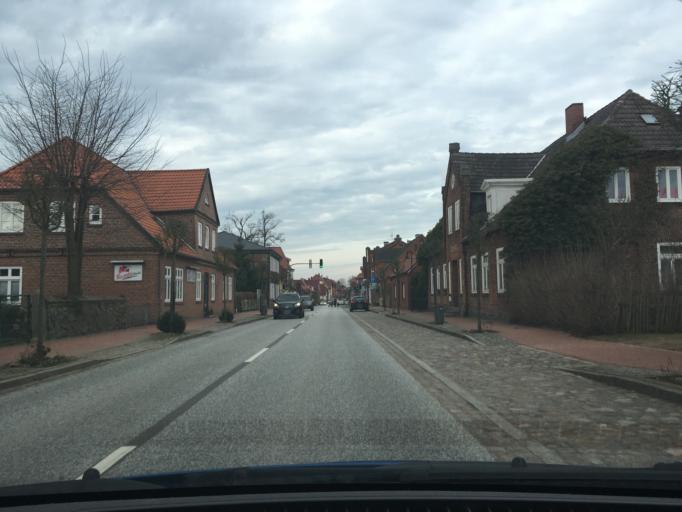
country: DE
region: Mecklenburg-Vorpommern
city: Zarrentin
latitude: 53.5500
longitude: 10.9163
